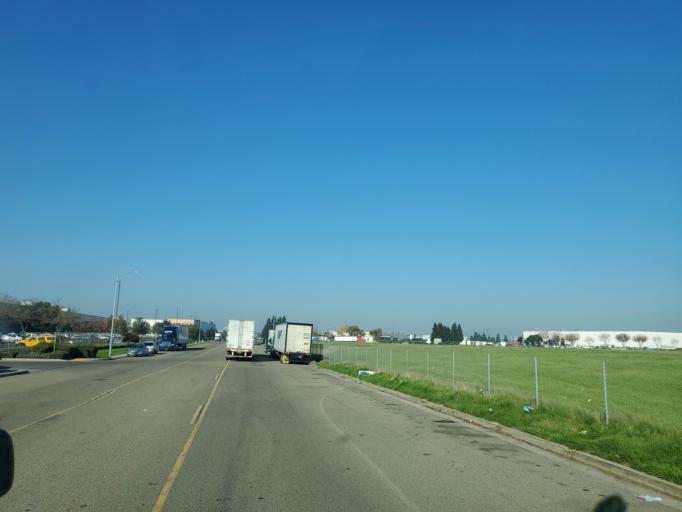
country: US
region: California
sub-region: San Joaquin County
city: French Camp
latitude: 37.8940
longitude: -121.2575
